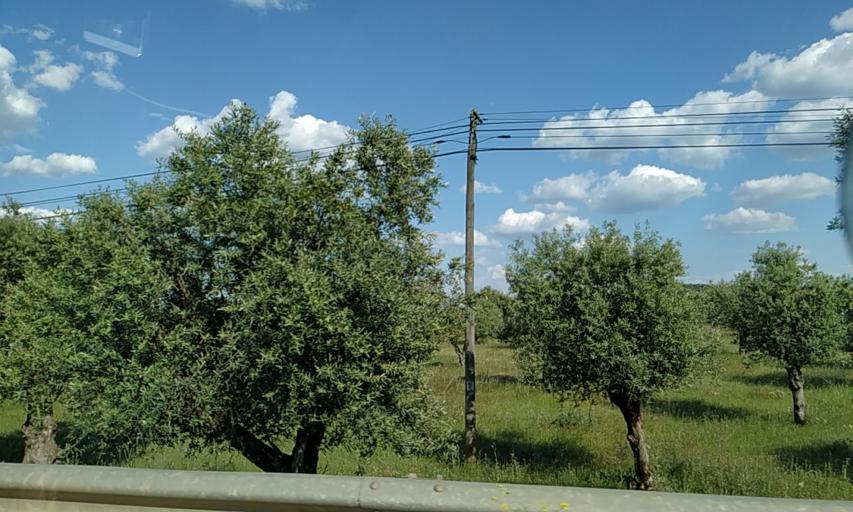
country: PT
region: Evora
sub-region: Estremoz
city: Estremoz
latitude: 38.8572
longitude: -7.5782
